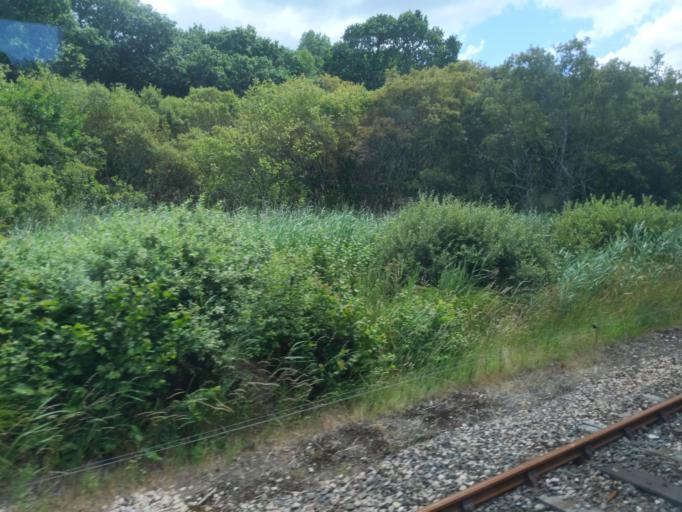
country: GB
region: England
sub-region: Cornwall
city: Par
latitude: 50.3596
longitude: -4.7022
